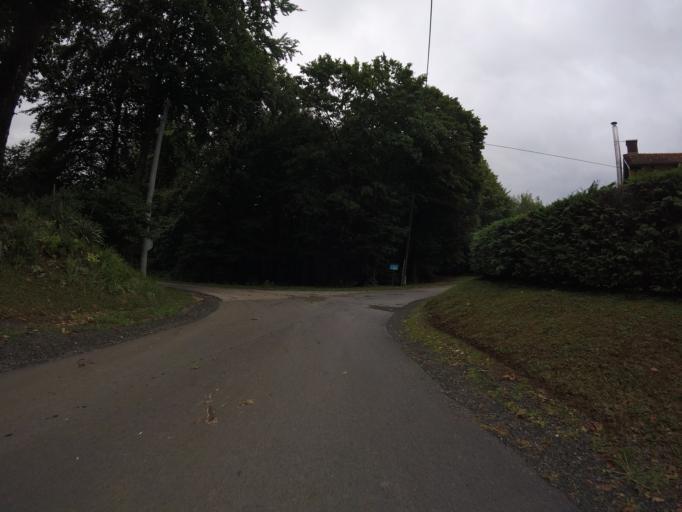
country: HR
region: Zagrebacka
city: Mraclin
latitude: 45.5967
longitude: 16.0795
